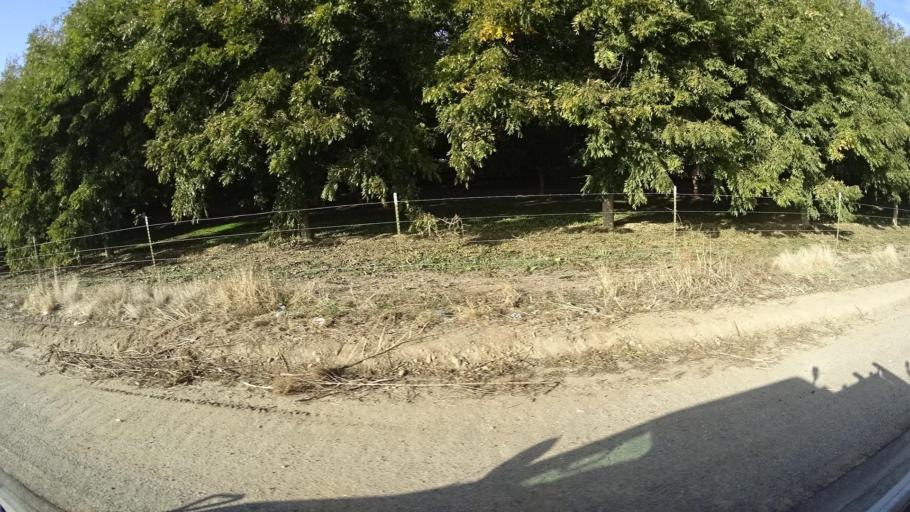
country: US
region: California
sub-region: Kern County
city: McFarland
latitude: 35.6328
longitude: -119.2045
